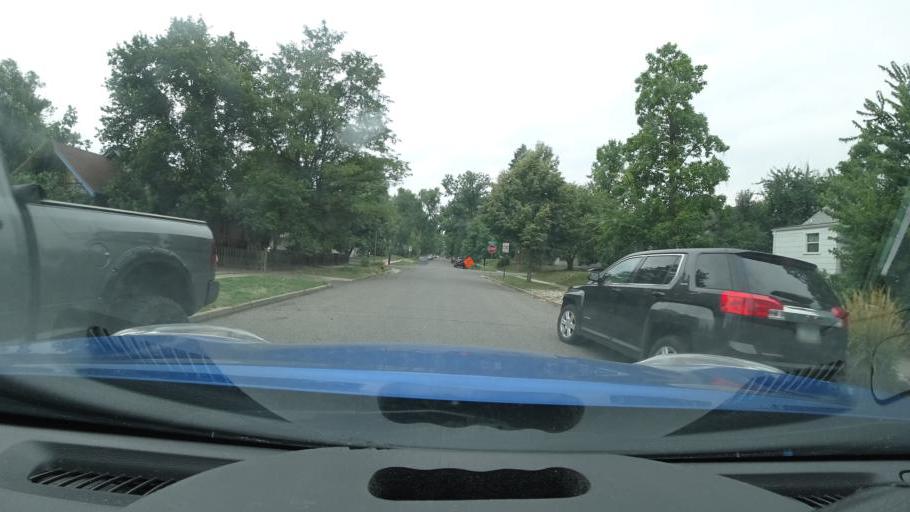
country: US
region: Colorado
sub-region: Arapahoe County
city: Glendale
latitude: 39.6826
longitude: -104.9664
